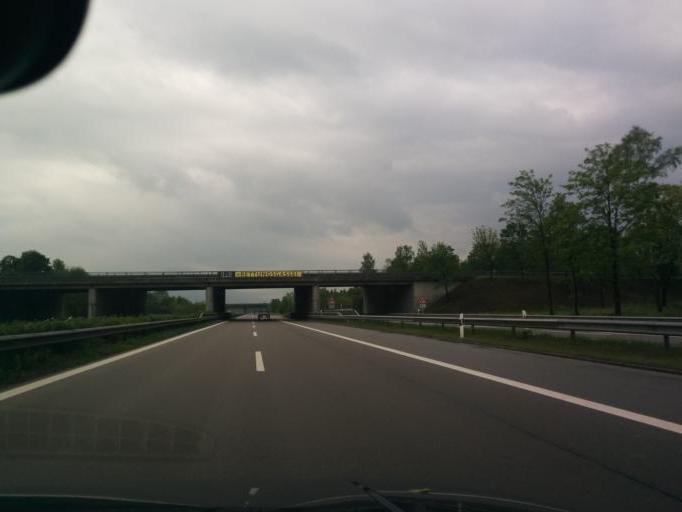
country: DE
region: Bavaria
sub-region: Upper Bavaria
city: Brunnthal
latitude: 48.0284
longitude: 11.6569
